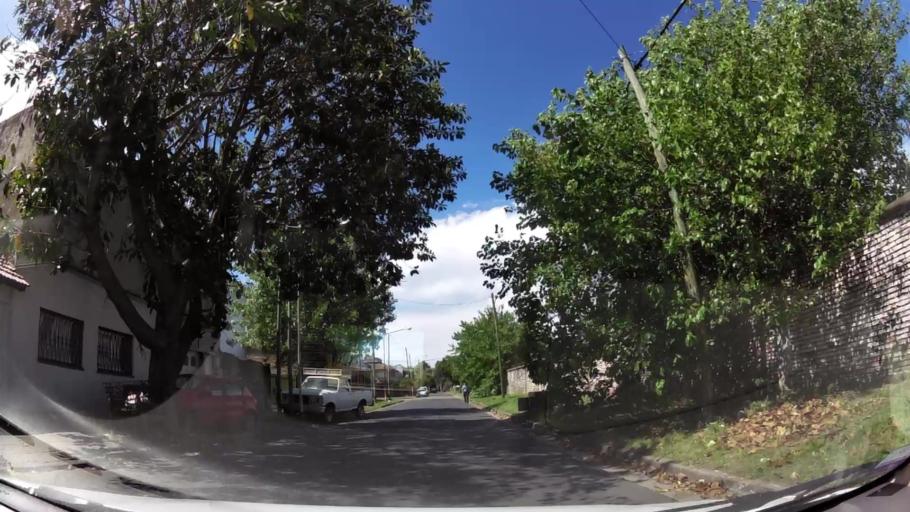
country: AR
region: Buenos Aires
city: San Justo
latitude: -34.6743
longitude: -58.5705
